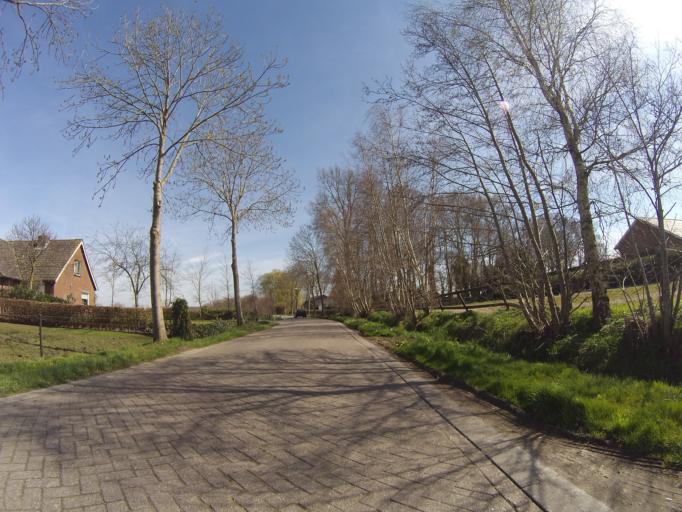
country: NL
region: Gelderland
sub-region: Gemeente Nijkerk
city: Nijkerk
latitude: 52.2049
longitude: 5.4908
